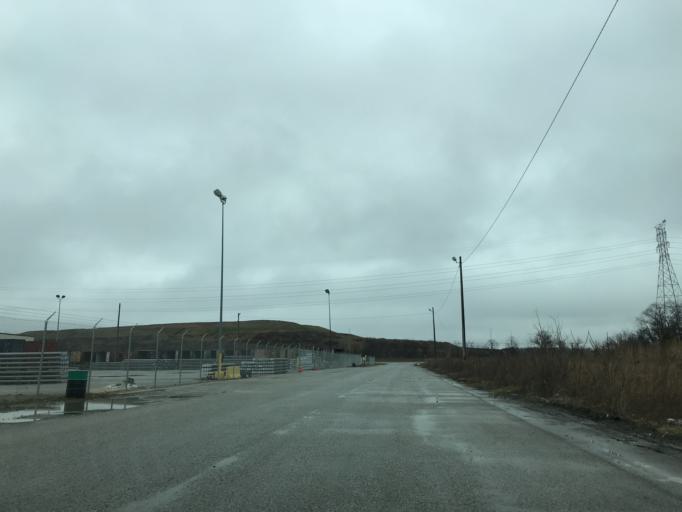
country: US
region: Maryland
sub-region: Baltimore County
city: Edgemere
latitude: 39.2361
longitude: -76.4821
